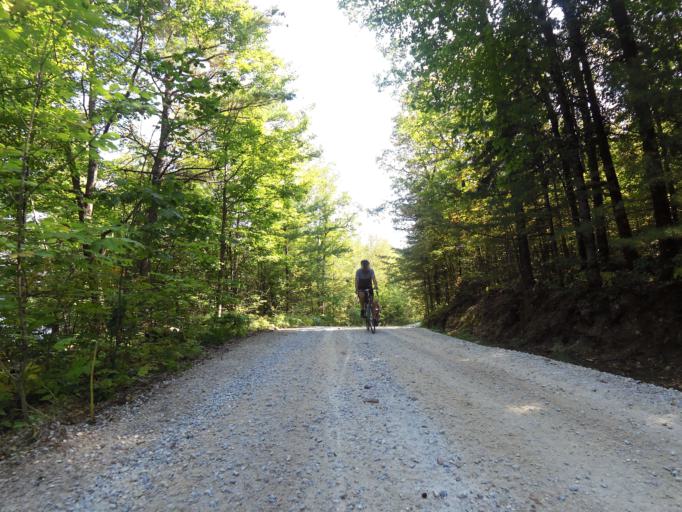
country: CA
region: Ontario
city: Perth
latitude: 45.0181
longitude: -76.6021
